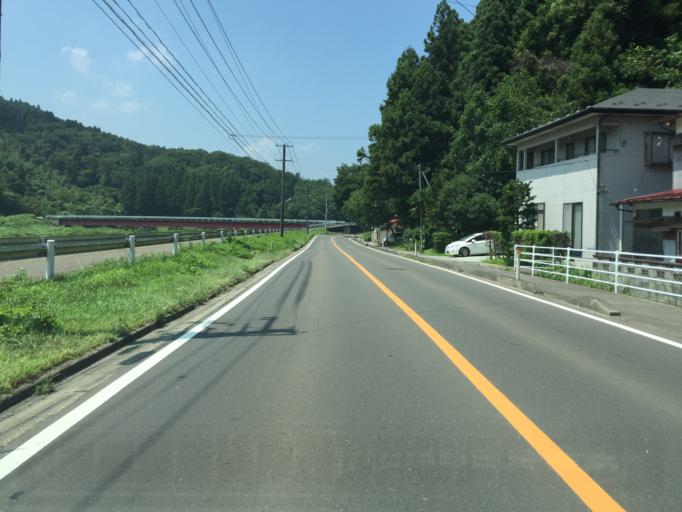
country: JP
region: Miyagi
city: Marumori
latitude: 37.8915
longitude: 140.8064
